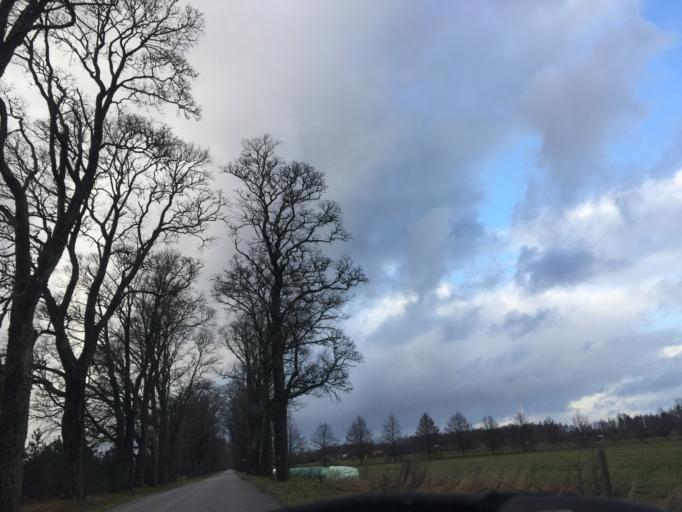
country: LV
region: Burtnieki
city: Matisi
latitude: 57.6866
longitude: 25.2876
